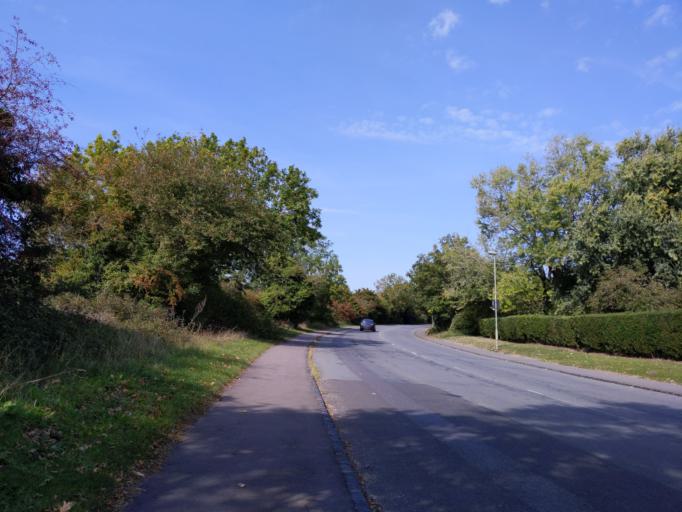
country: GB
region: England
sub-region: Oxfordshire
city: Radley
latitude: 51.7140
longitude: -1.2290
